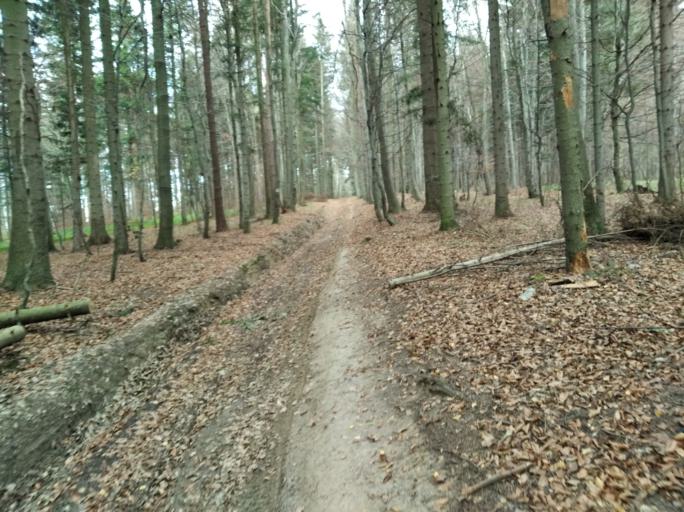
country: PL
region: Subcarpathian Voivodeship
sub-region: Powiat strzyzowski
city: Jawornik
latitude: 49.8599
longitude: 21.8541
